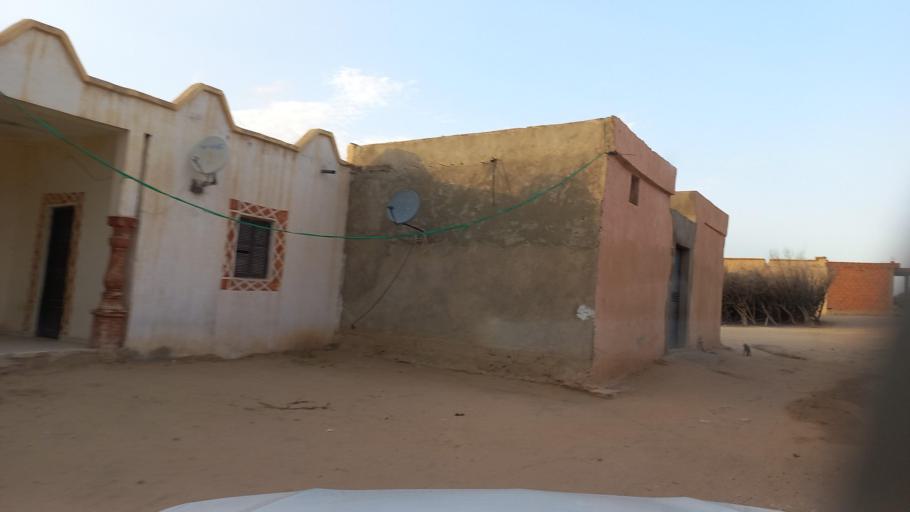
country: TN
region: Al Qasrayn
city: Kasserine
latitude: 35.2705
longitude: 9.0678
